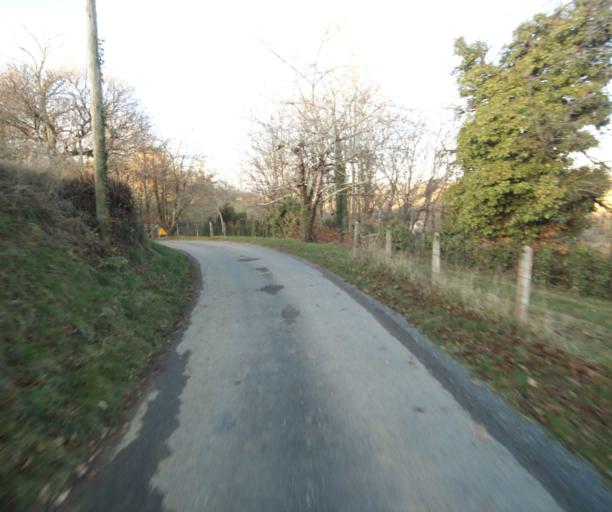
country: FR
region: Limousin
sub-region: Departement de la Correze
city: Laguenne
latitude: 45.2297
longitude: 1.8282
